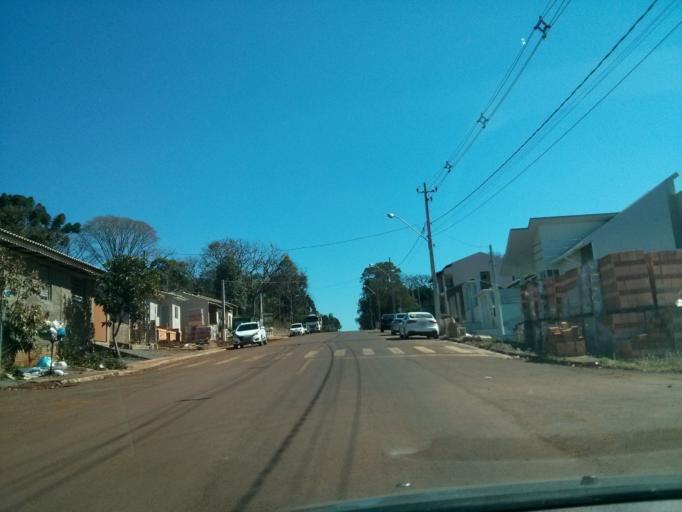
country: BR
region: Santa Catarina
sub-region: Chapeco
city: Chapeco
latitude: -27.0902
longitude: -52.6868
